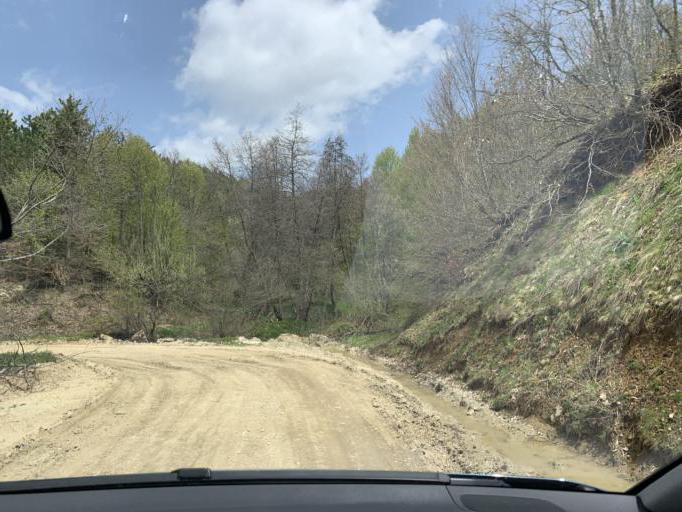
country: TR
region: Bolu
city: Bolu
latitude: 40.8324
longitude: 31.6741
